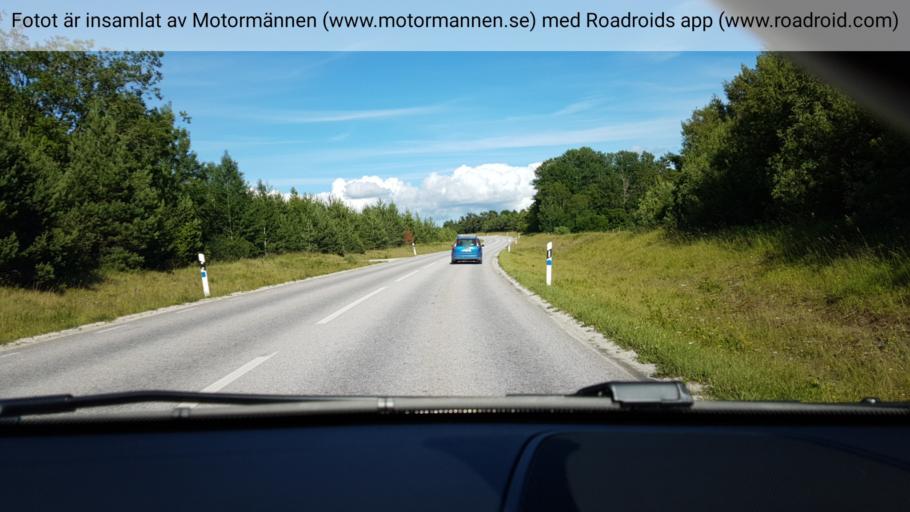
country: SE
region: Gotland
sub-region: Gotland
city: Slite
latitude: 57.7431
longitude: 18.6398
